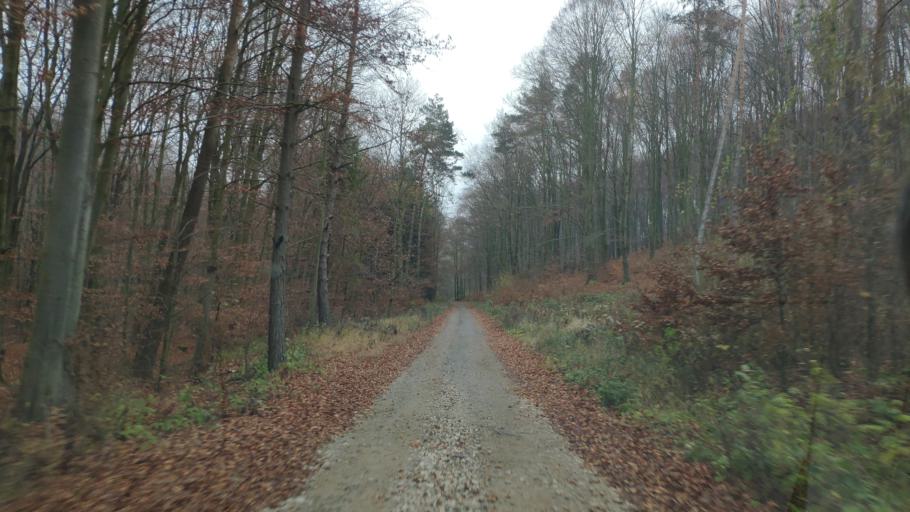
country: SK
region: Presovsky
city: Sabinov
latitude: 49.1497
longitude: 21.2082
